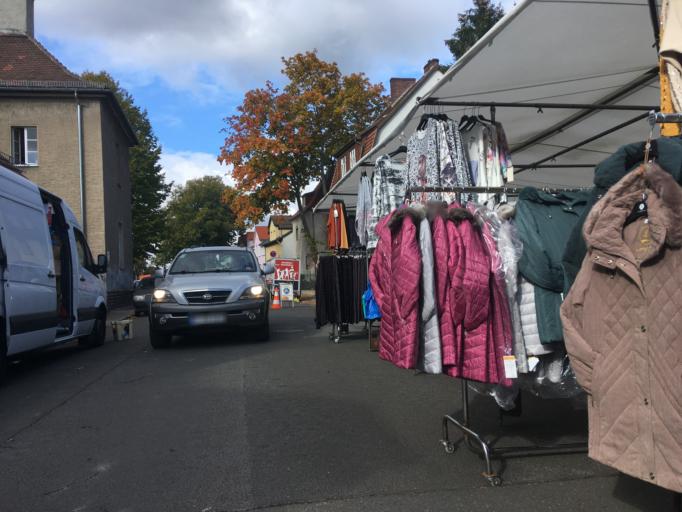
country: DE
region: Berlin
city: Rudow
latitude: 52.4201
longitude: 13.4964
